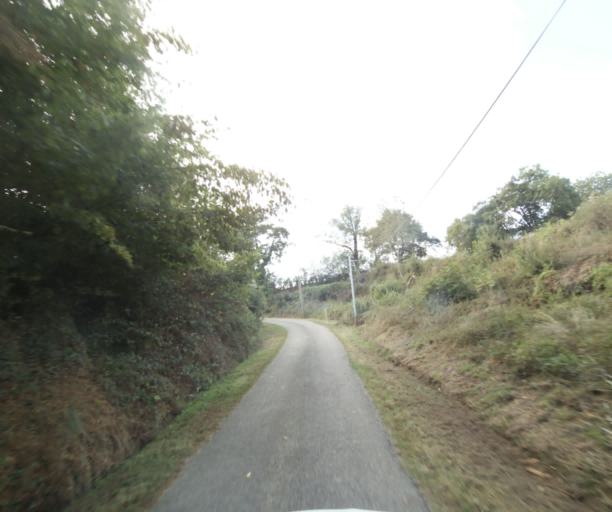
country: FR
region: Bourgogne
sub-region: Departement de Saone-et-Loire
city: Charolles
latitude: 46.4610
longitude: 4.3853
